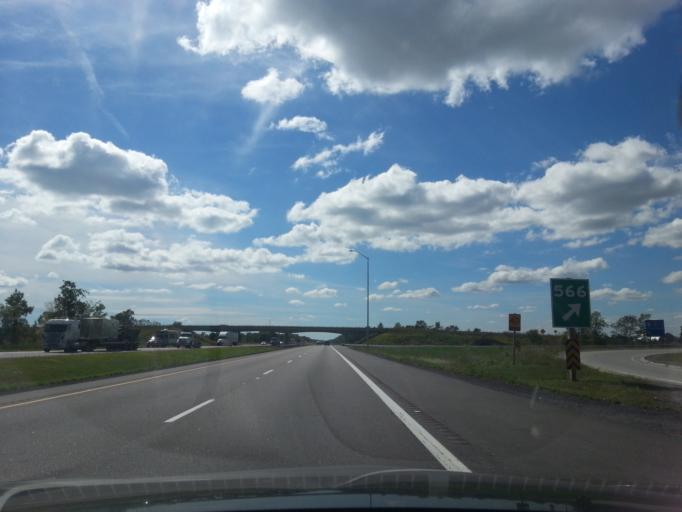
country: CA
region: Ontario
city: Deseronto
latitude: 44.2380
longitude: -77.1111
